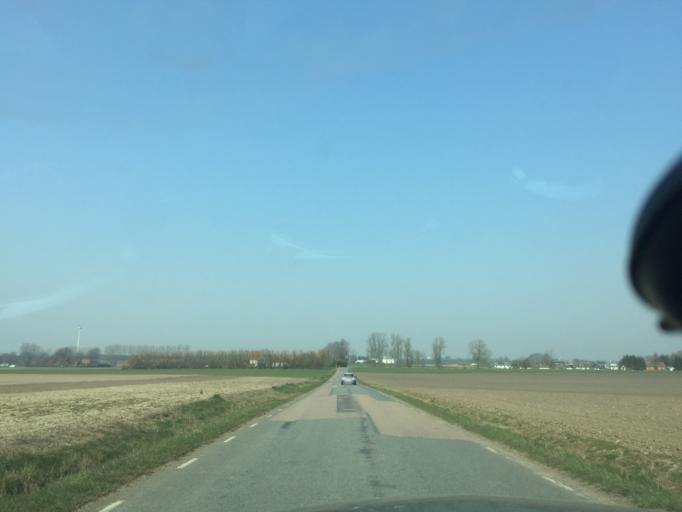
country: SE
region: Skane
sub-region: Simrishamns Kommun
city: Simrishamn
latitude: 55.4622
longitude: 14.2104
